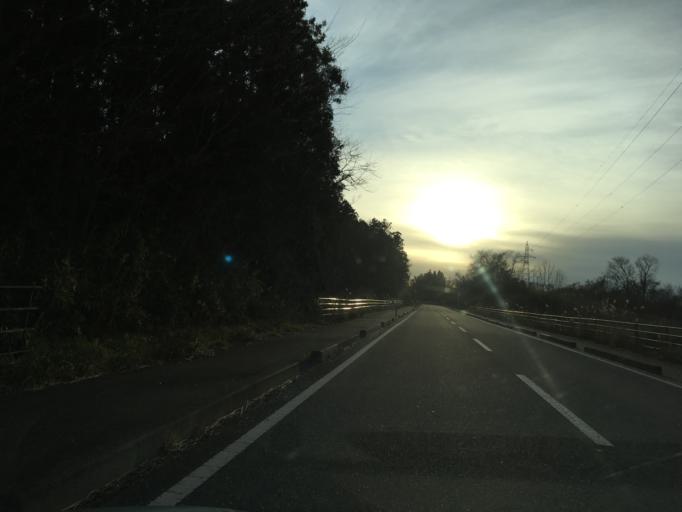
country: JP
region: Miyagi
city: Wakuya
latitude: 38.7170
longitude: 141.1332
